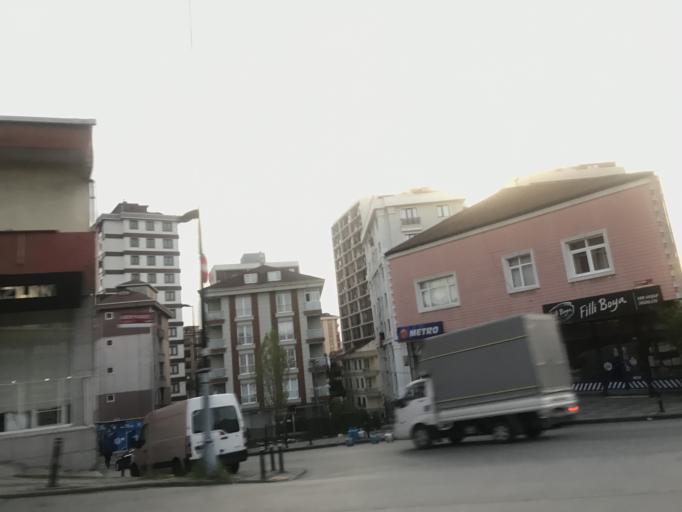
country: TR
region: Istanbul
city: Umraniye
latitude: 41.0367
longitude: 29.1014
